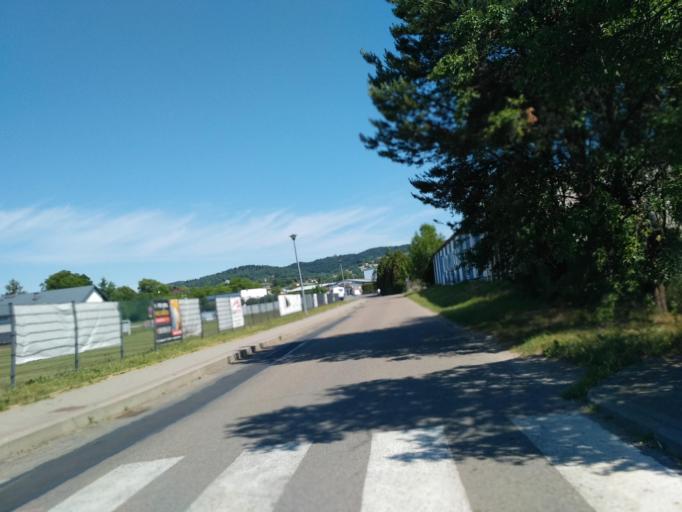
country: PL
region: Subcarpathian Voivodeship
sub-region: Powiat krosnienski
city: Korczyna
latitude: 49.7136
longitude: 21.8067
